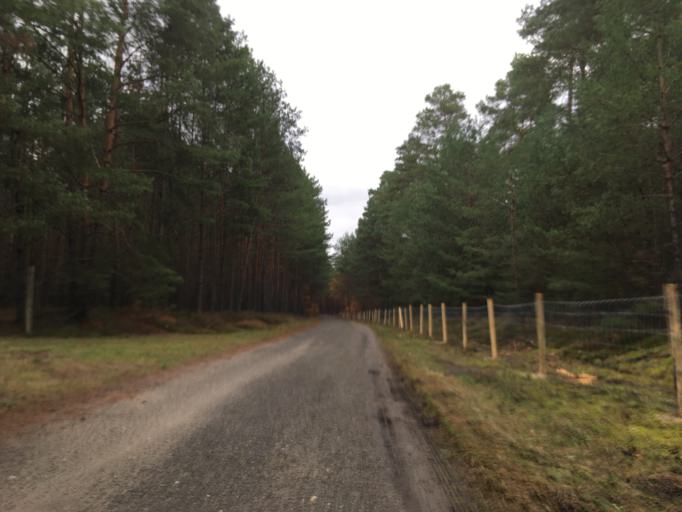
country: DE
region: Brandenburg
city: Jamlitz
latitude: 52.0618
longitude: 14.4816
